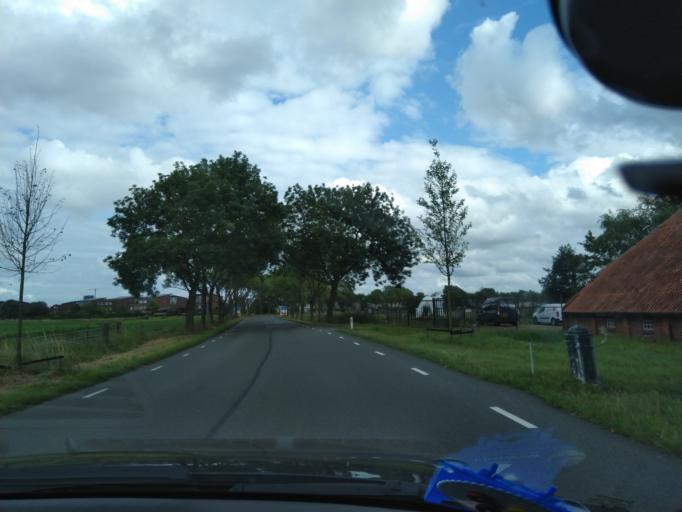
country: NL
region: Groningen
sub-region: Gemeente Zuidhorn
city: Aduard
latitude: 53.2364
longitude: 6.4965
